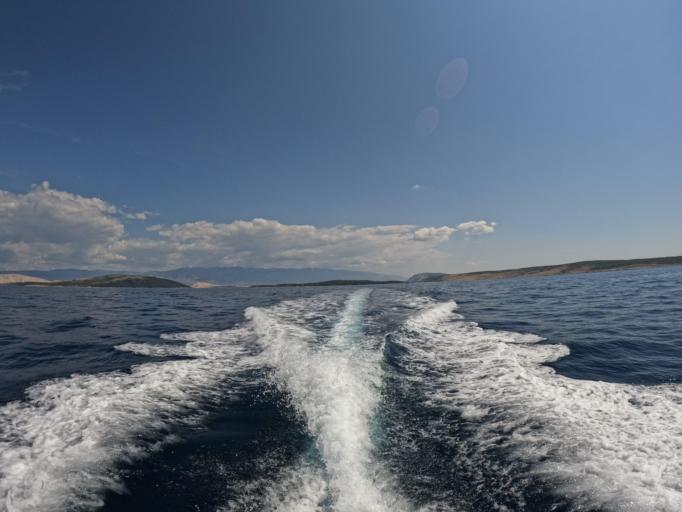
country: HR
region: Primorsko-Goranska
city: Lopar
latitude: 44.8632
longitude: 14.6900
